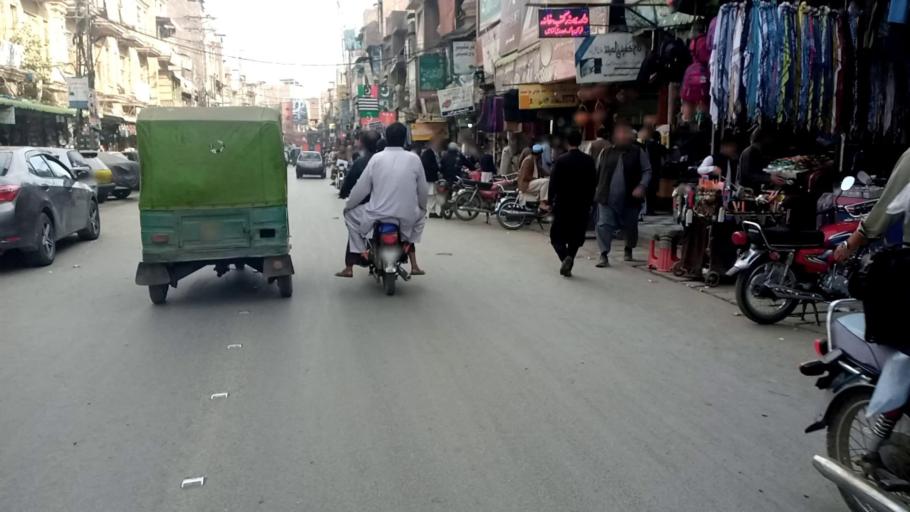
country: PK
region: Khyber Pakhtunkhwa
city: Peshawar
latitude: 34.0082
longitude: 71.5692
